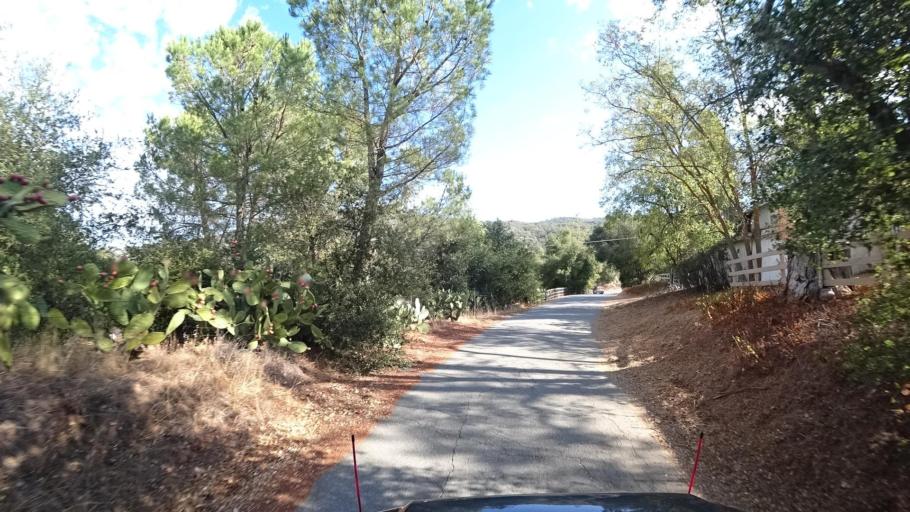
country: US
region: California
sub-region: San Diego County
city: San Diego Country Estates
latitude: 33.1713
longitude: -116.7600
